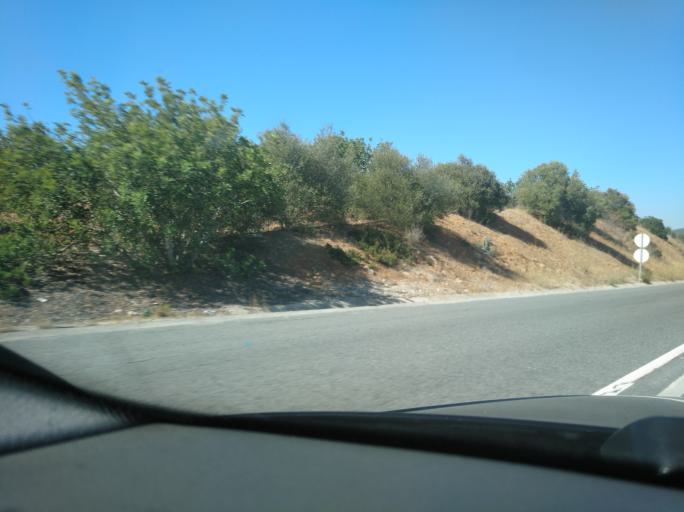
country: PT
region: Faro
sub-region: Olhao
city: Laranjeiro
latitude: 37.0721
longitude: -7.8089
